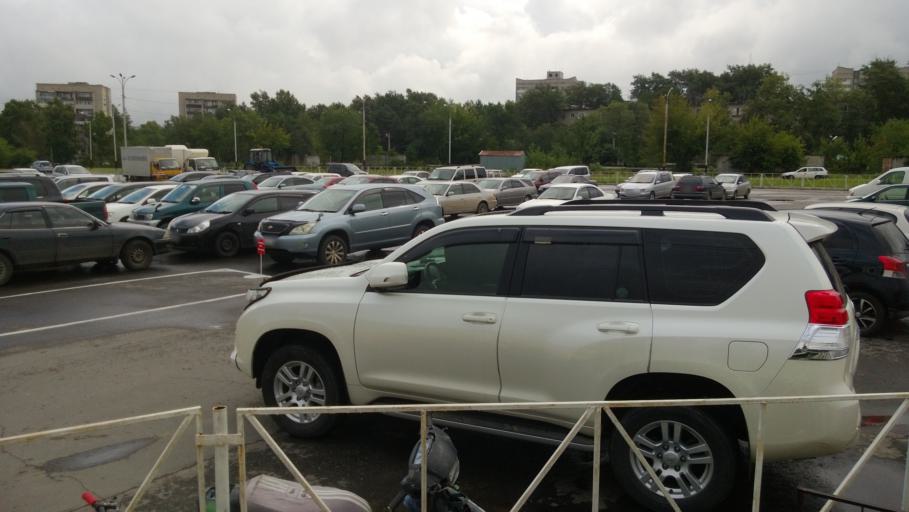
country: RU
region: Khabarovsk Krai
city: Khabarovsk Vtoroy
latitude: 48.3945
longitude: 135.1062
